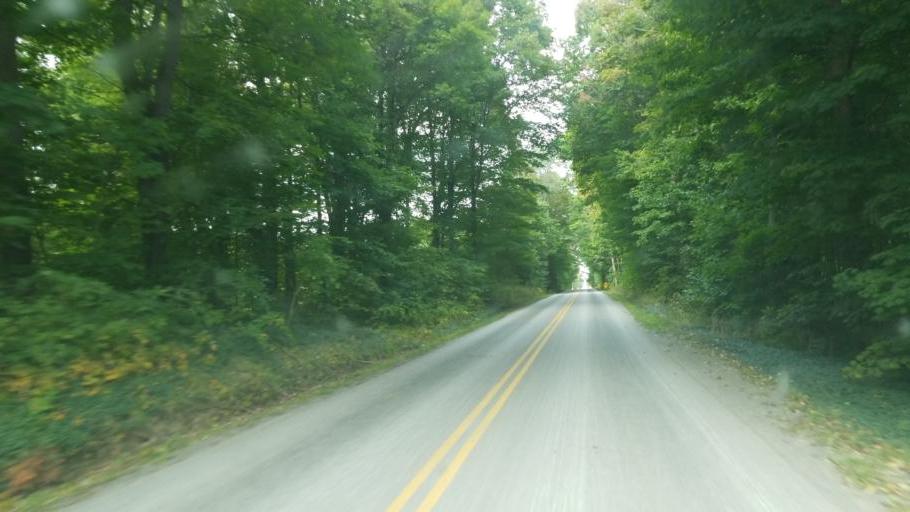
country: US
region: Pennsylvania
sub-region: Mercer County
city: Greenville
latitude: 41.4948
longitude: -80.3383
